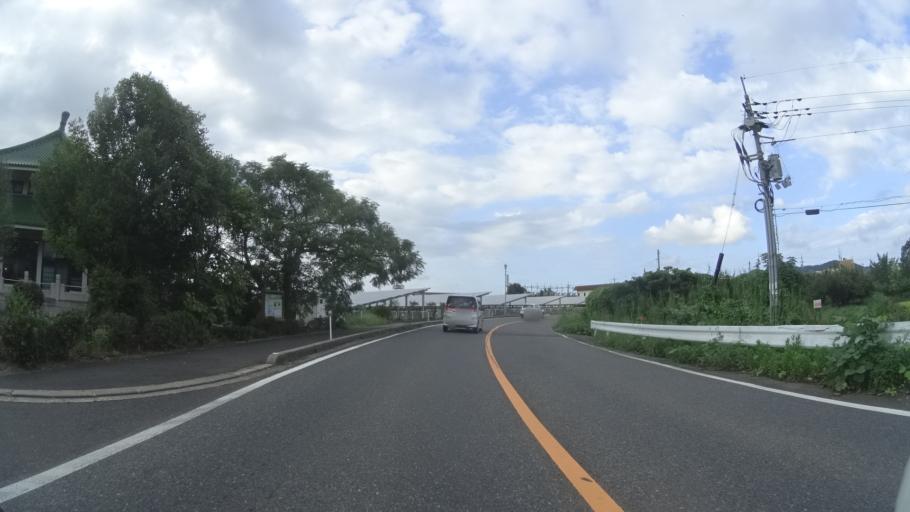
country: JP
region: Tottori
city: Kurayoshi
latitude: 35.4663
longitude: 133.8945
